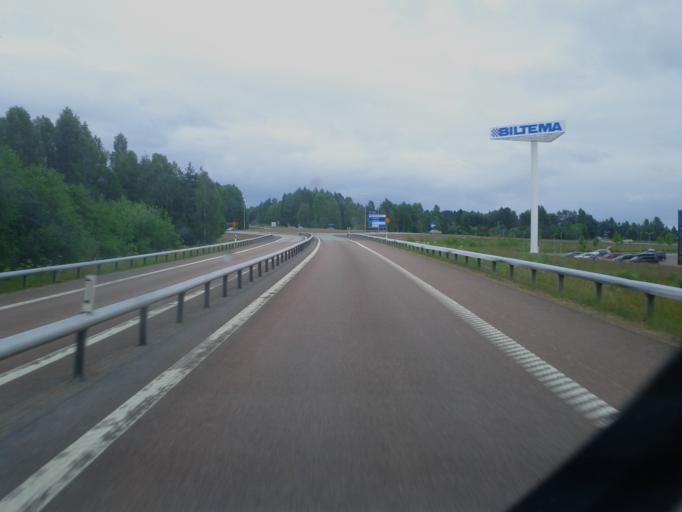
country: SE
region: Dalarna
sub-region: Mora Kommun
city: Mora
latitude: 61.0077
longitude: 14.6025
